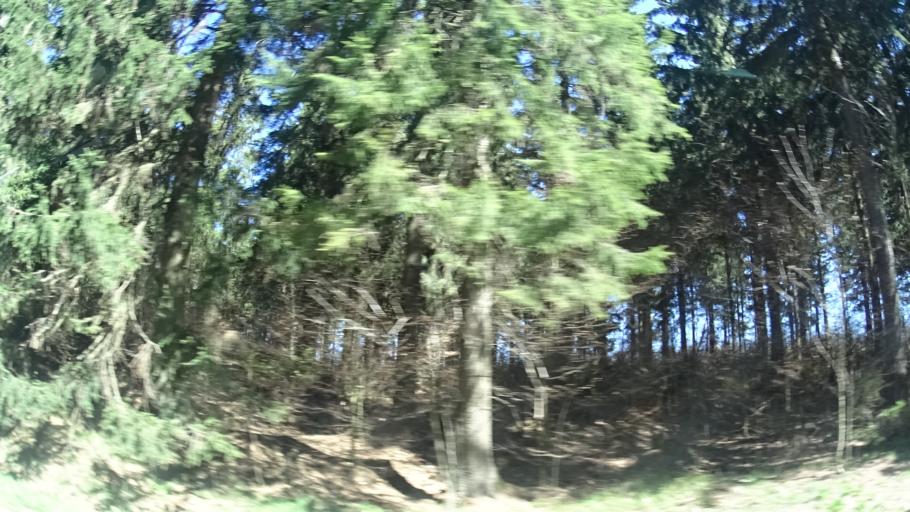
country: DE
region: Thuringia
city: Altenfeld
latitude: 50.5934
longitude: 10.9607
